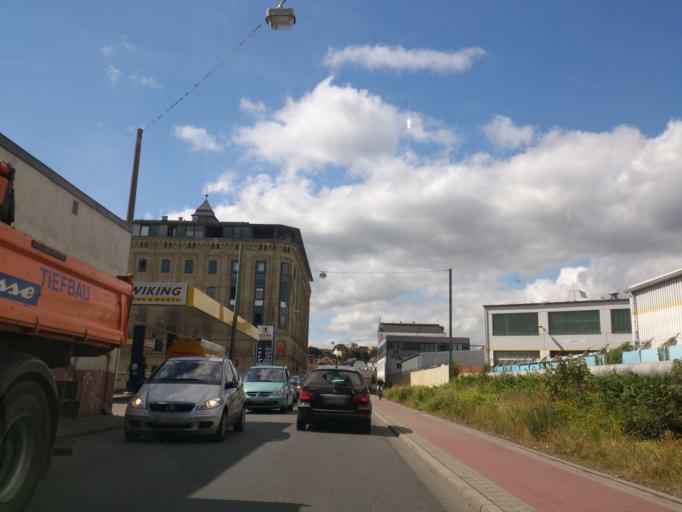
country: DE
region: Schleswig-Holstein
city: Flensburg
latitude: 54.7965
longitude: 9.4302
